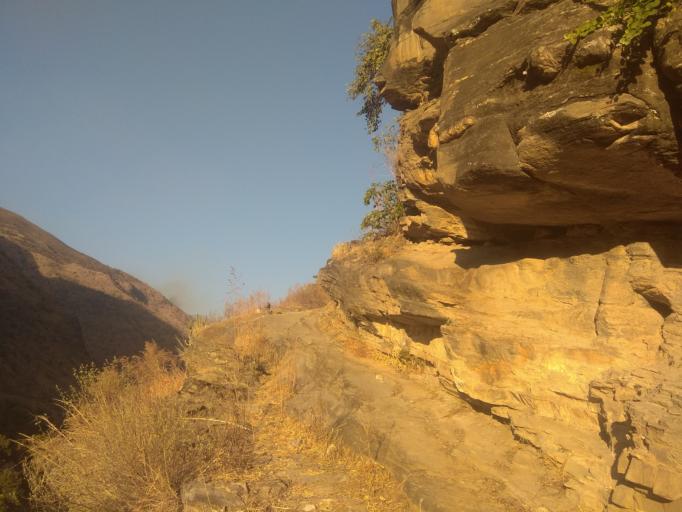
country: NP
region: Mid Western
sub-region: Bheri Zone
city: Dailekh
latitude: 29.2778
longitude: 81.7313
